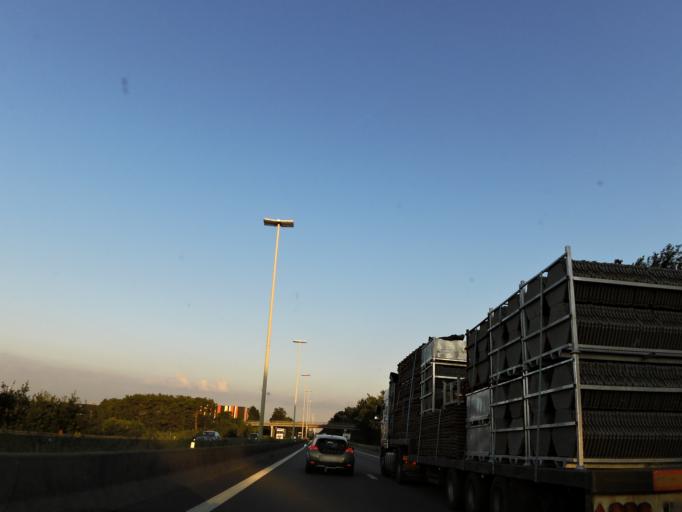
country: BE
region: Flanders
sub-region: Provincie Antwerpen
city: Olen
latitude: 51.1482
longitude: 4.8697
